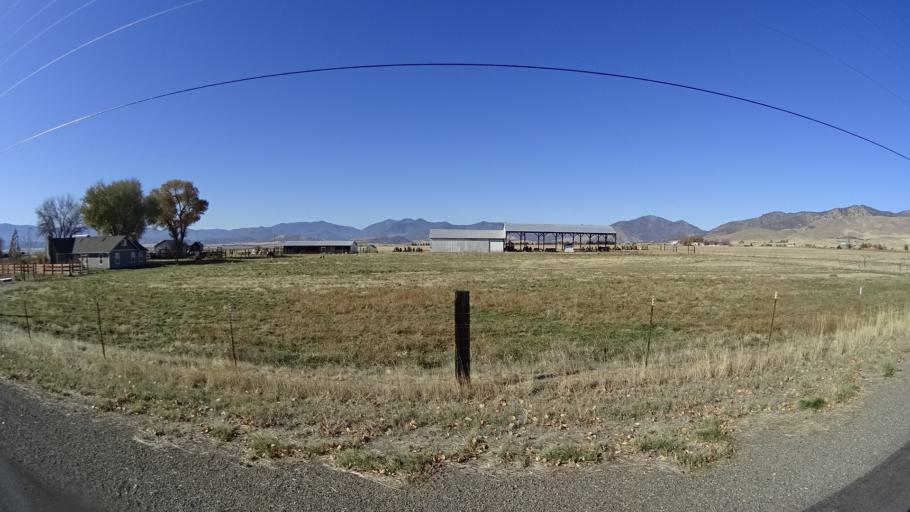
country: US
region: California
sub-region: Siskiyou County
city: Montague
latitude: 41.7577
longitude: -122.5247
